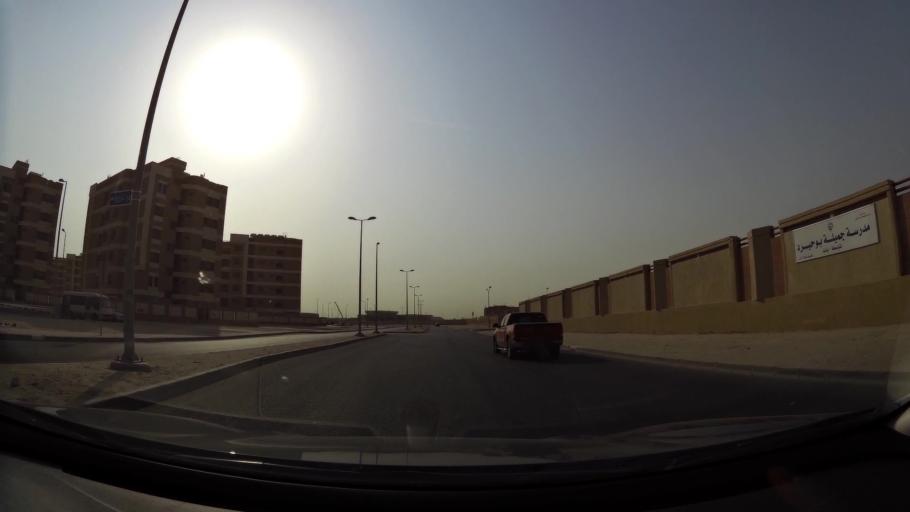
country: KW
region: Al Asimah
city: Ar Rabiyah
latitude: 29.3242
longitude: 47.8163
